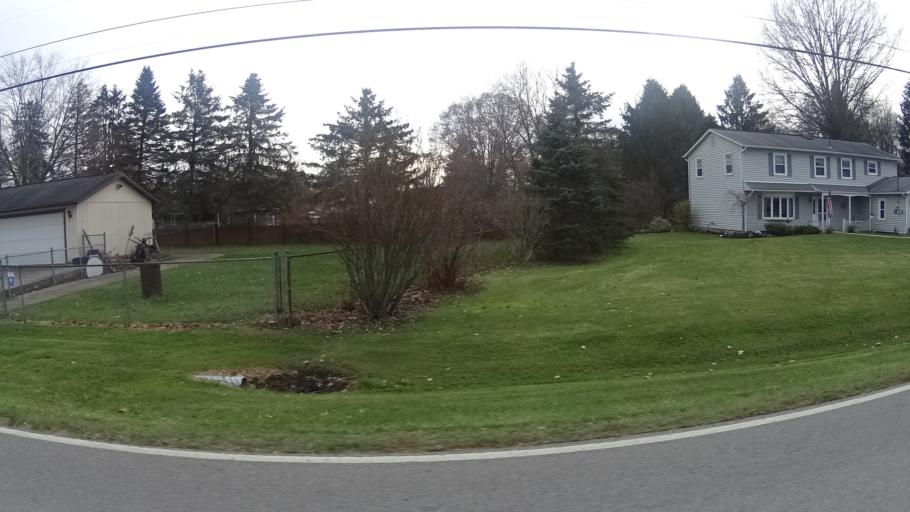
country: US
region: Ohio
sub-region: Lorain County
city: Eaton Estates
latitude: 41.2895
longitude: -81.9319
